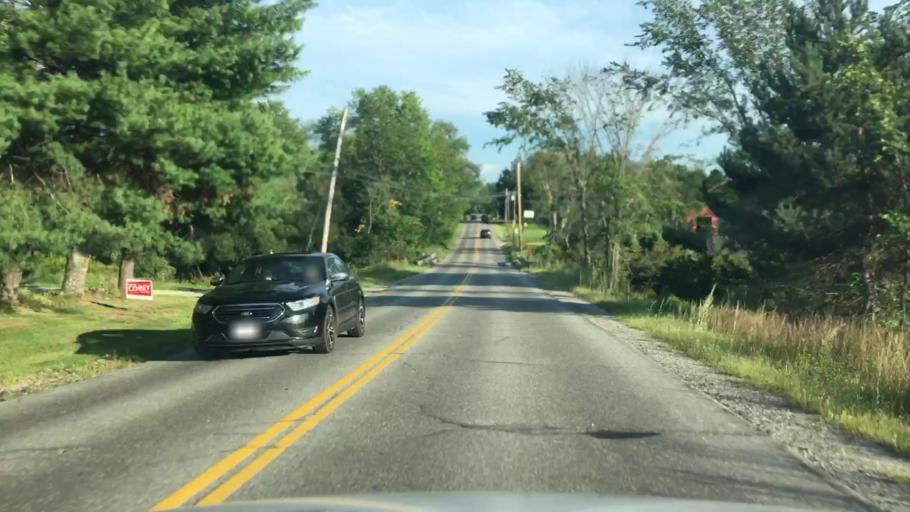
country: US
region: Maine
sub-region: Cumberland County
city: South Windham
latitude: 43.7270
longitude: -70.4069
